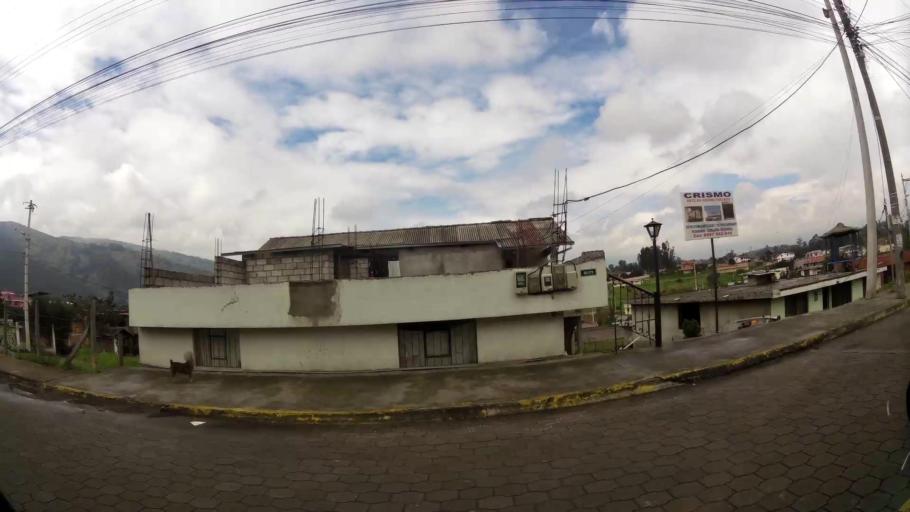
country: EC
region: Pichincha
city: Sangolqui
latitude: -0.3017
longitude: -78.4386
